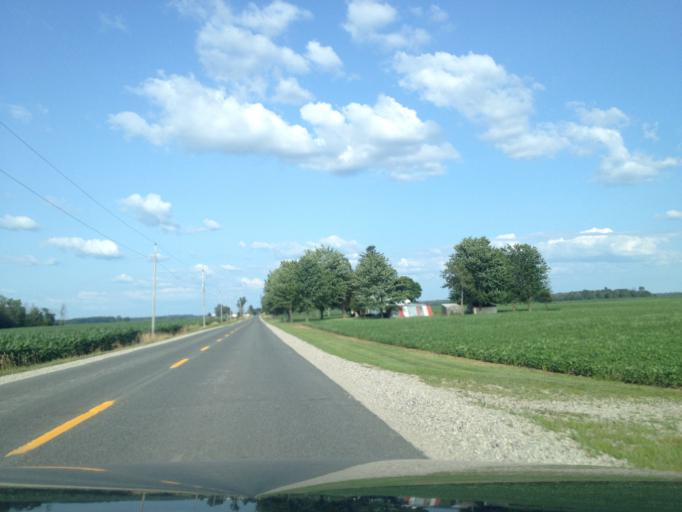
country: CA
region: Ontario
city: Ingersoll
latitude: 42.9658
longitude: -80.7441
